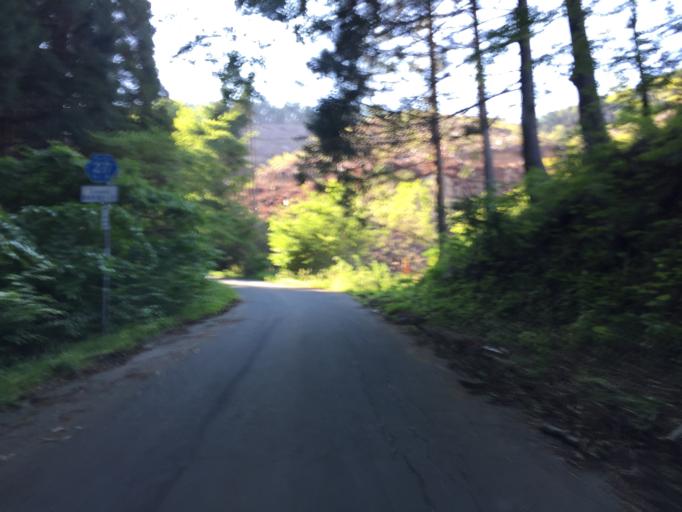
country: JP
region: Ibaraki
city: Kitaibaraki
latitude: 36.8711
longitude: 140.6734
